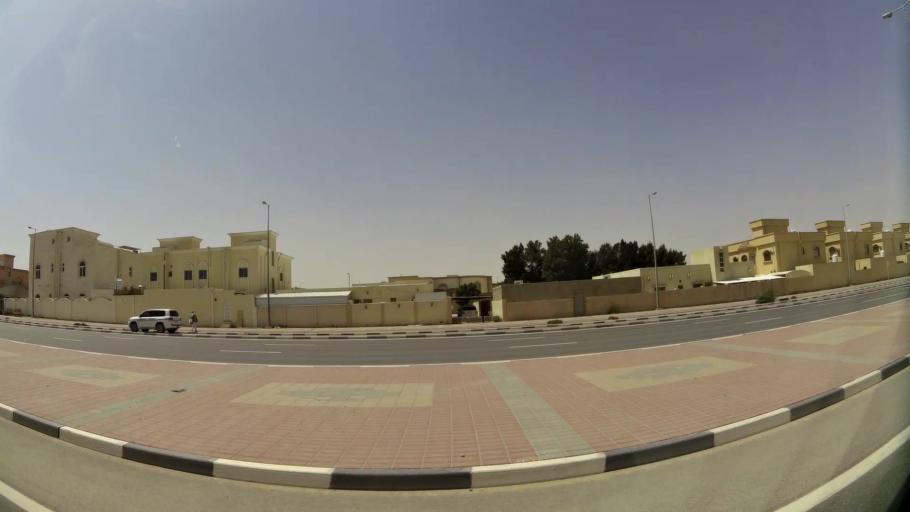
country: QA
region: Baladiyat Umm Salal
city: Umm Salal Muhammad
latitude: 25.4010
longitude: 51.4578
